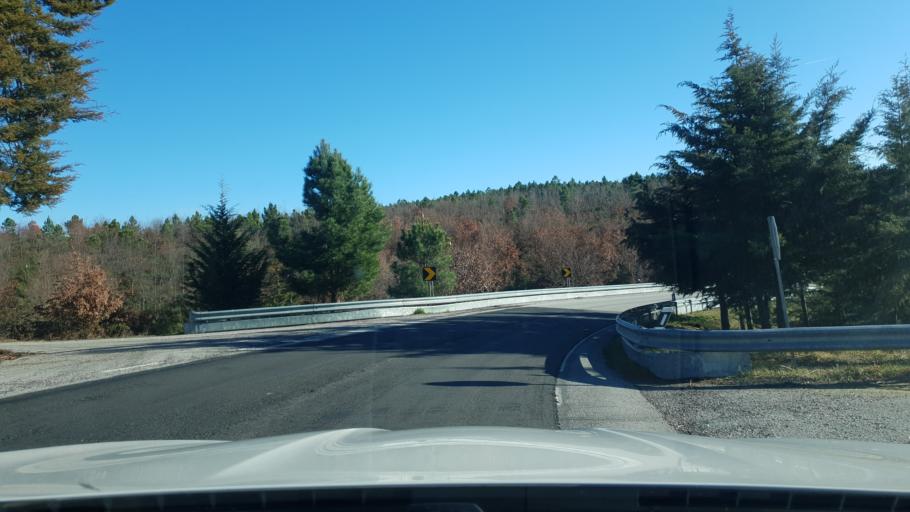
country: PT
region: Braganca
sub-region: Freixo de Espada A Cinta
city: Freixo de Espada a Cinta
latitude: 41.1380
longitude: -6.8058
